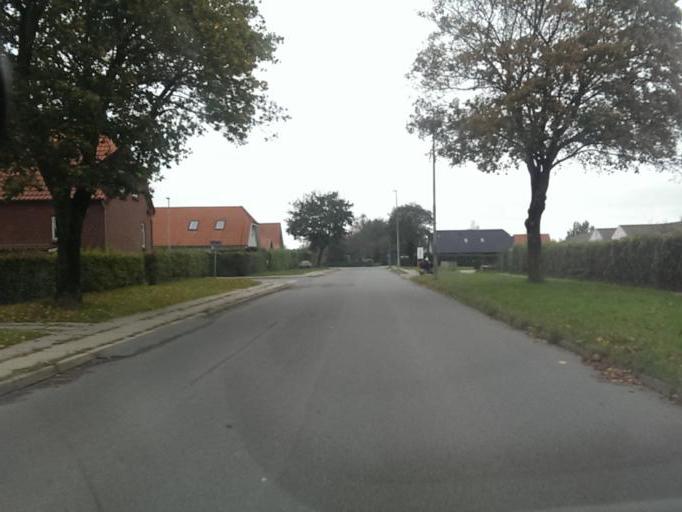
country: DK
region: South Denmark
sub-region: Esbjerg Kommune
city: Bramming
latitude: 55.4681
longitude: 8.7115
